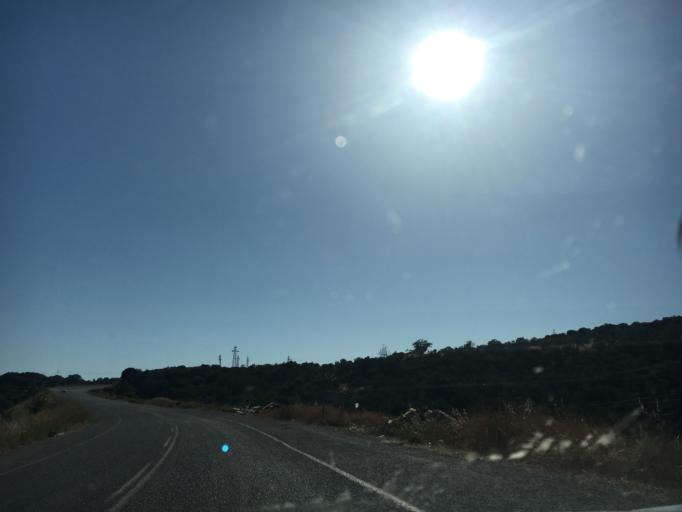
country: TR
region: Canakkale
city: Behram
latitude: 39.5067
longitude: 26.4058
